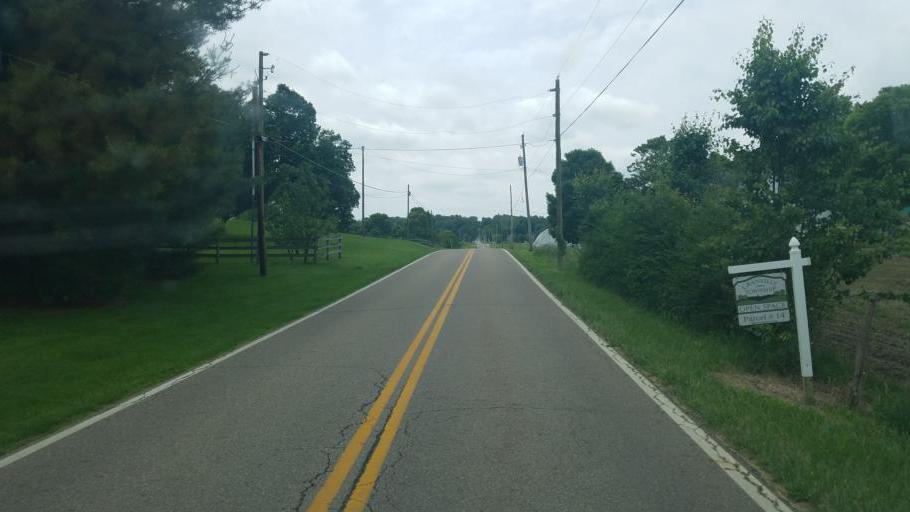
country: US
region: Ohio
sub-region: Licking County
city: Granville
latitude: 40.0934
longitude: -82.5395
